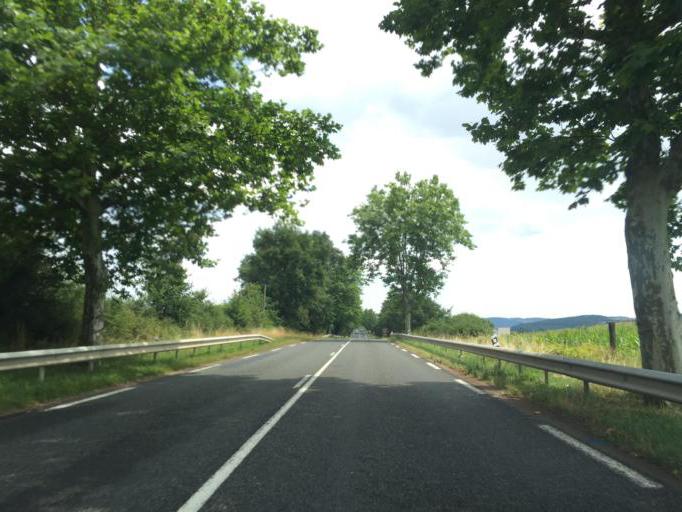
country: FR
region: Rhone-Alpes
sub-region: Departement du Rhone
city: Saint-Romain-de-Popey
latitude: 45.8714
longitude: 4.5398
